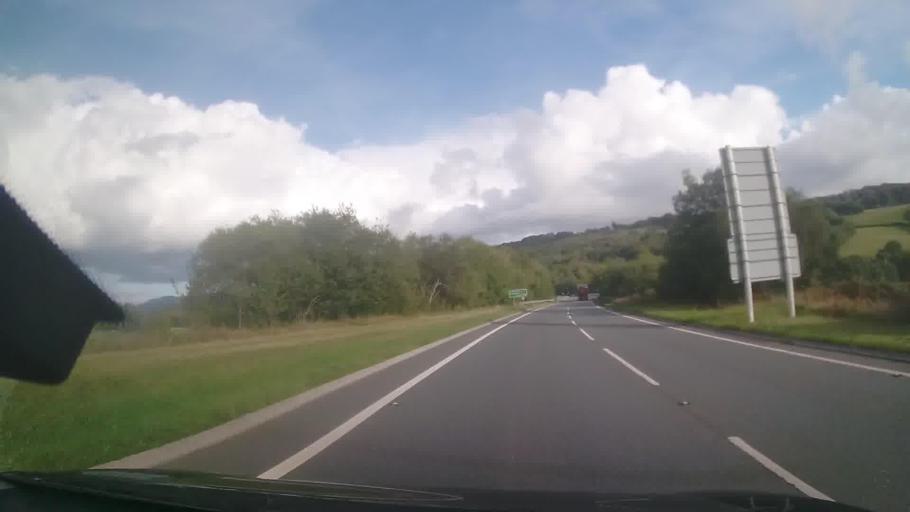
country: GB
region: Wales
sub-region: Gwynedd
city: Dolgellau
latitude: 52.7453
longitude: -3.8746
